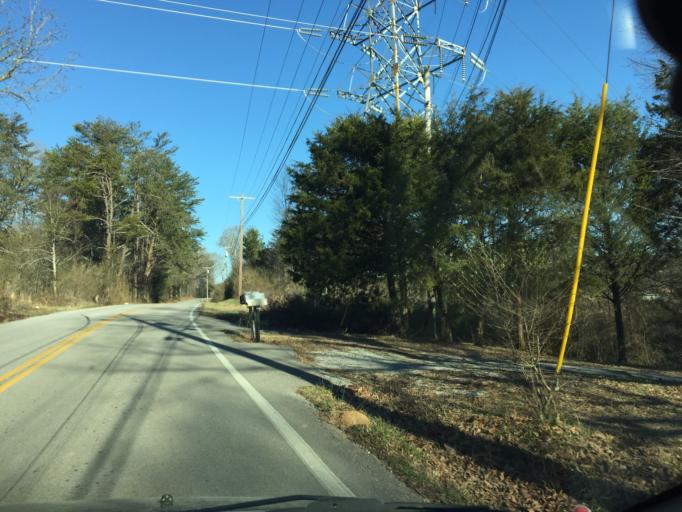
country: US
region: Tennessee
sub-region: Hamilton County
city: Collegedale
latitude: 35.0604
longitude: -85.0953
